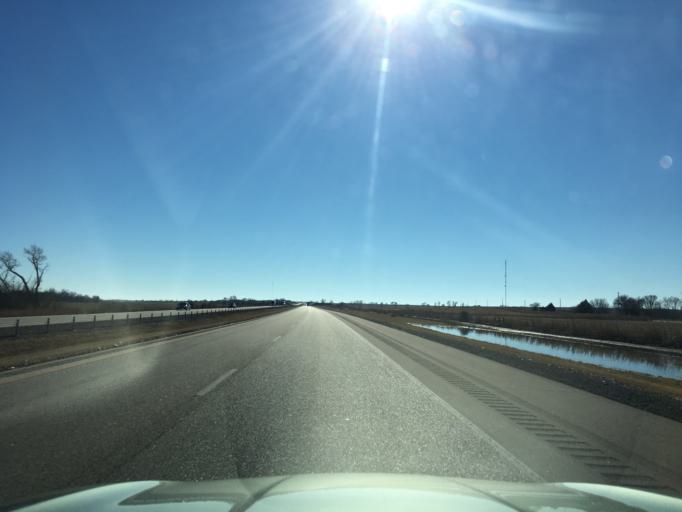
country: US
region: Oklahoma
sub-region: Kay County
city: Blackwell
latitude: 36.8935
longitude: -97.3539
